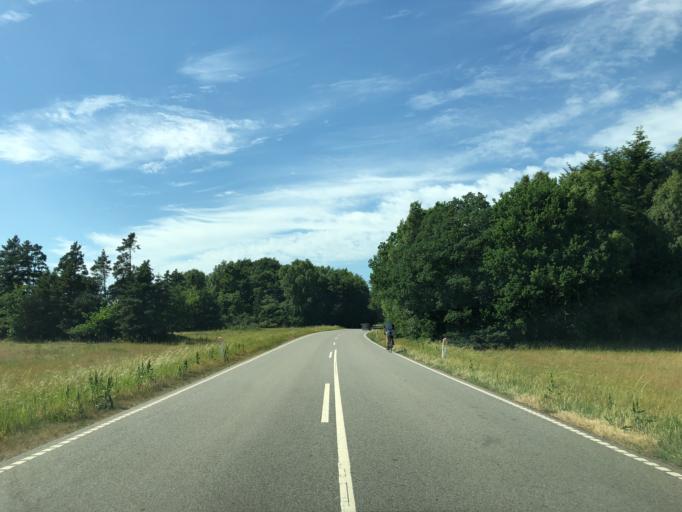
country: DK
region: Central Jutland
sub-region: Ikast-Brande Kommune
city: Brande
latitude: 55.9178
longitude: 9.1706
